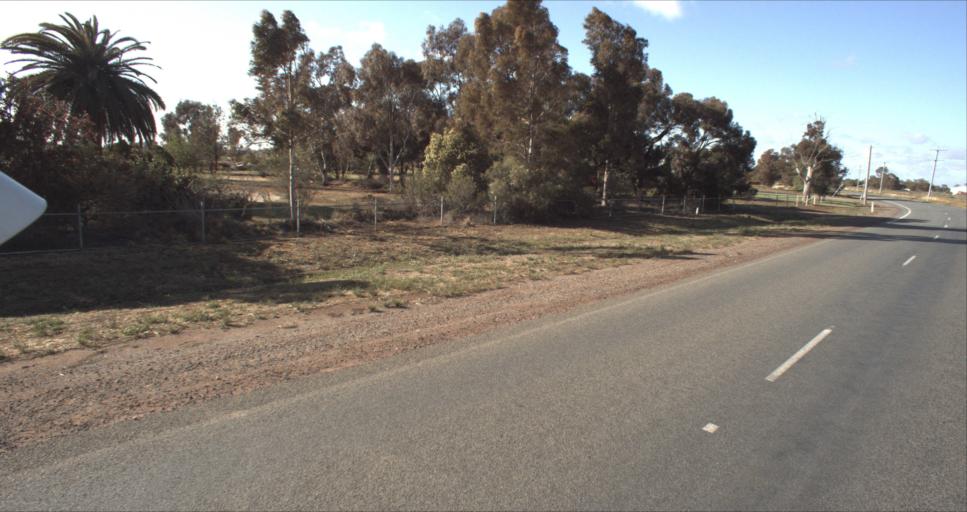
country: AU
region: New South Wales
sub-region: Leeton
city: Leeton
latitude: -34.5378
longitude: 146.3877
